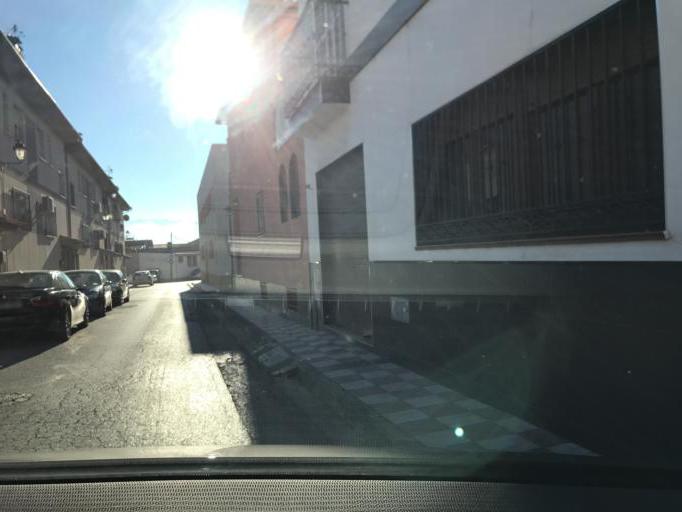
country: ES
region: Andalusia
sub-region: Provincia de Granada
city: Albolote
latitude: 37.2340
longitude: -3.6559
